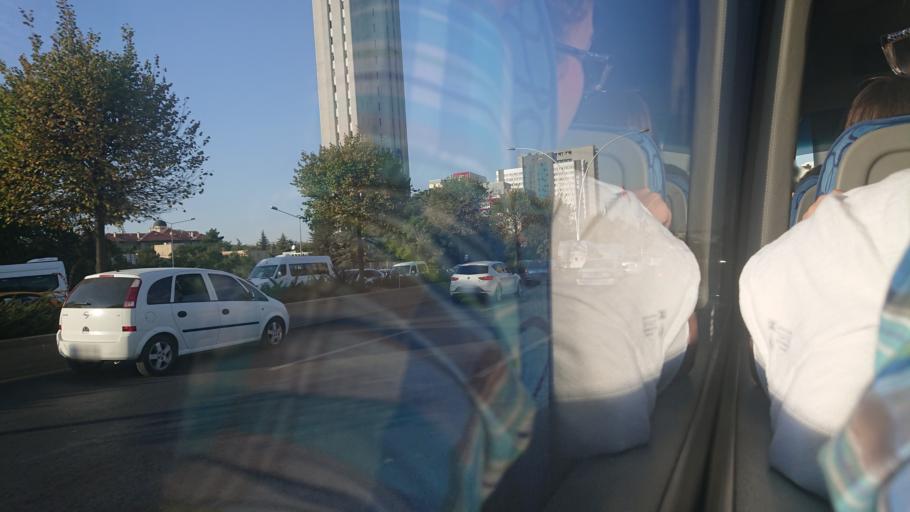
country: TR
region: Ankara
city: Ankara
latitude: 39.9366
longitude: 32.8236
